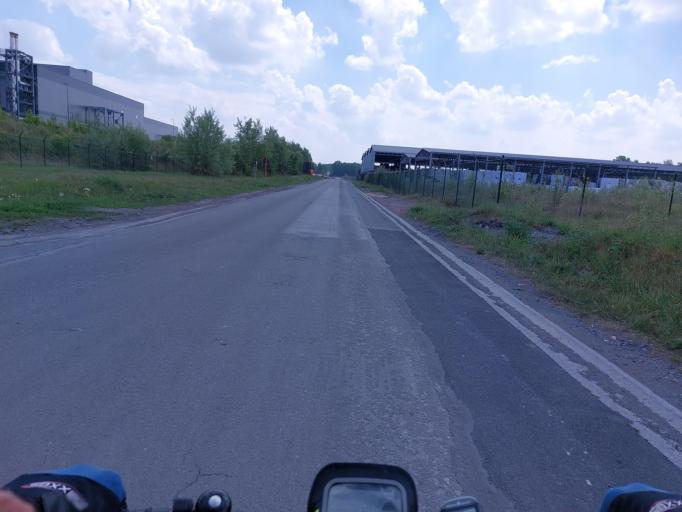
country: BE
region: Wallonia
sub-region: Province du Hainaut
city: Quaregnon
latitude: 50.4662
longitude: 3.8581
